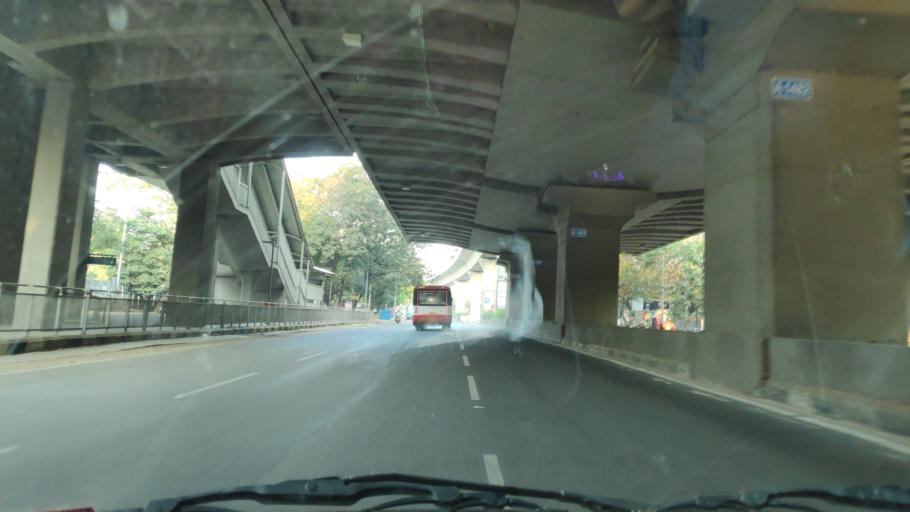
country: IN
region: Telangana
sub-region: Rangareddi
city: Gaddi Annaram
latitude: 17.3711
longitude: 78.5119
